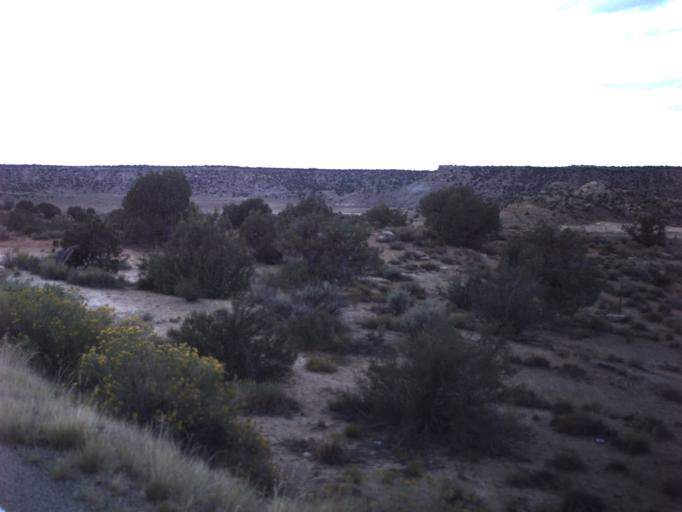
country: US
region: Utah
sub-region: San Juan County
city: Blanding
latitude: 37.4341
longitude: -109.3971
